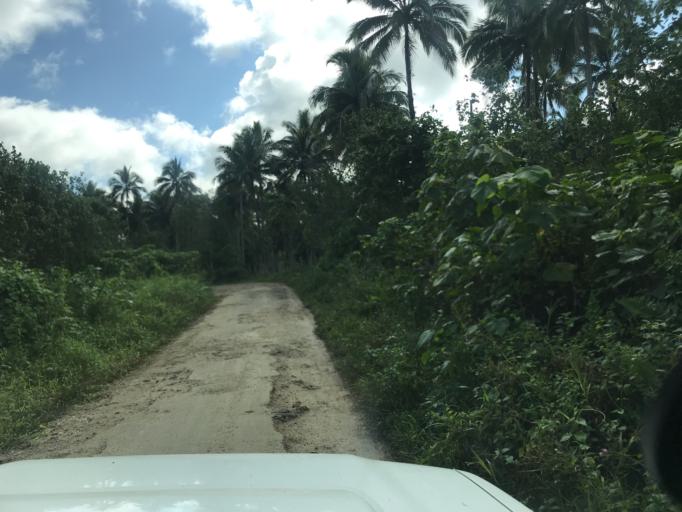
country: VU
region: Sanma
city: Luganville
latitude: -15.4700
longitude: 167.0734
